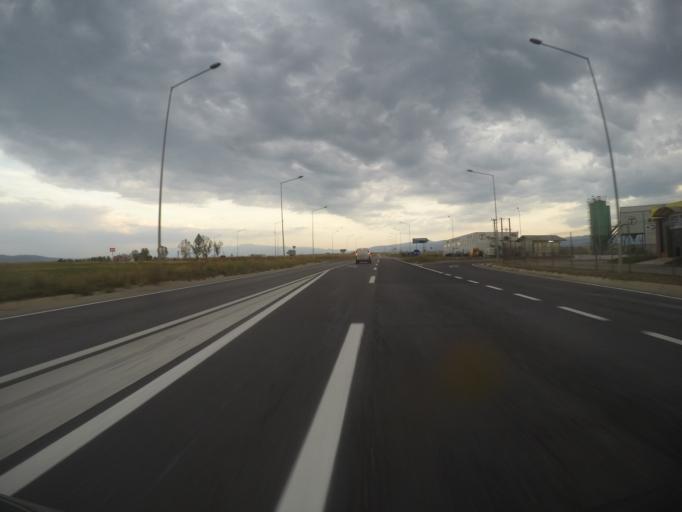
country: RO
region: Sibiu
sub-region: Comuna Sura Mica
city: Sura Mica
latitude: 45.8116
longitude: 24.0736
